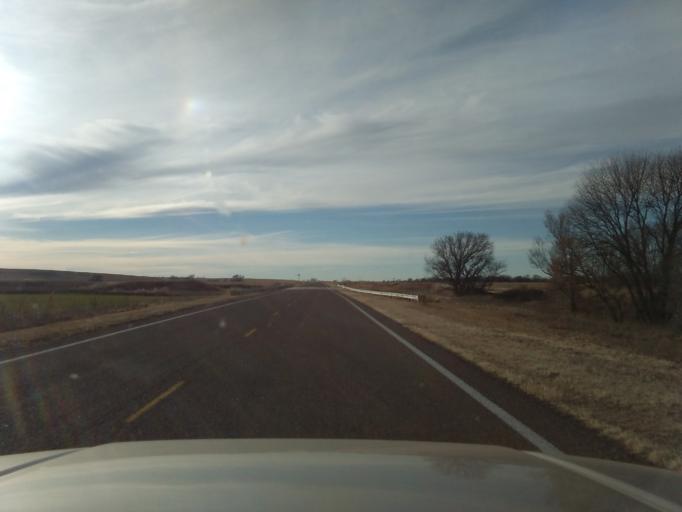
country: US
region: Kansas
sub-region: Norton County
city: Norton
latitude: 39.7565
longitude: -100.1166
